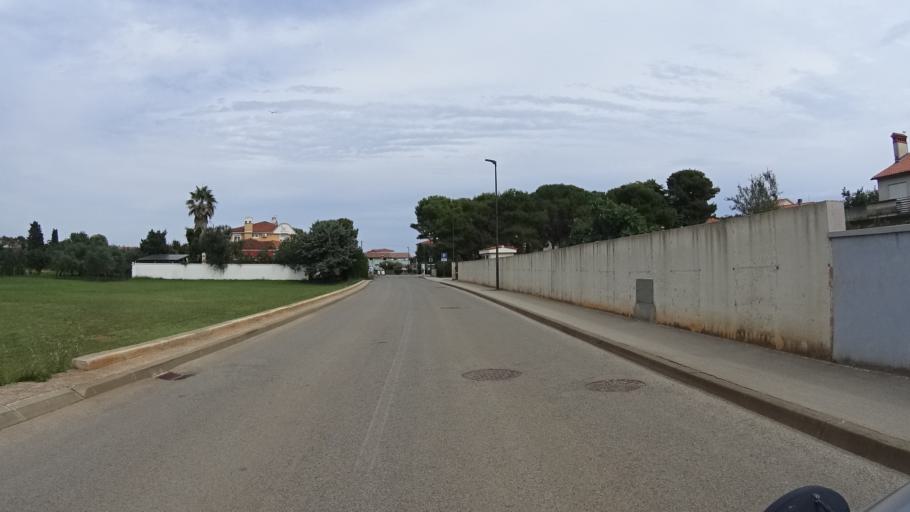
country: HR
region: Istarska
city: Medulin
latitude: 44.8246
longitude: 13.8944
